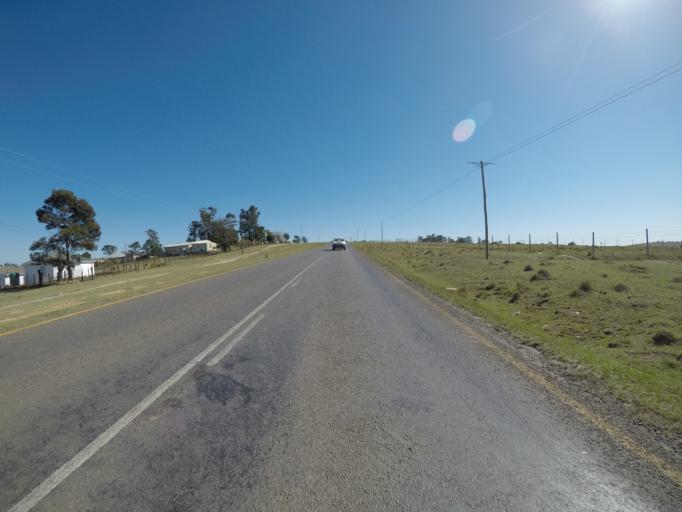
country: ZA
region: Eastern Cape
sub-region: OR Tambo District Municipality
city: Mthatha
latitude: -31.7951
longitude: 28.7449
